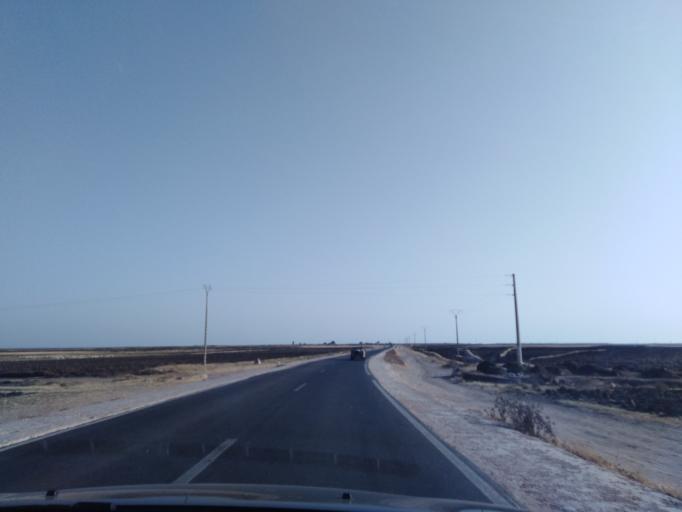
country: MA
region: Doukkala-Abda
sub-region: El-Jadida
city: Sidi Bennour
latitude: 32.5349
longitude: -8.7308
